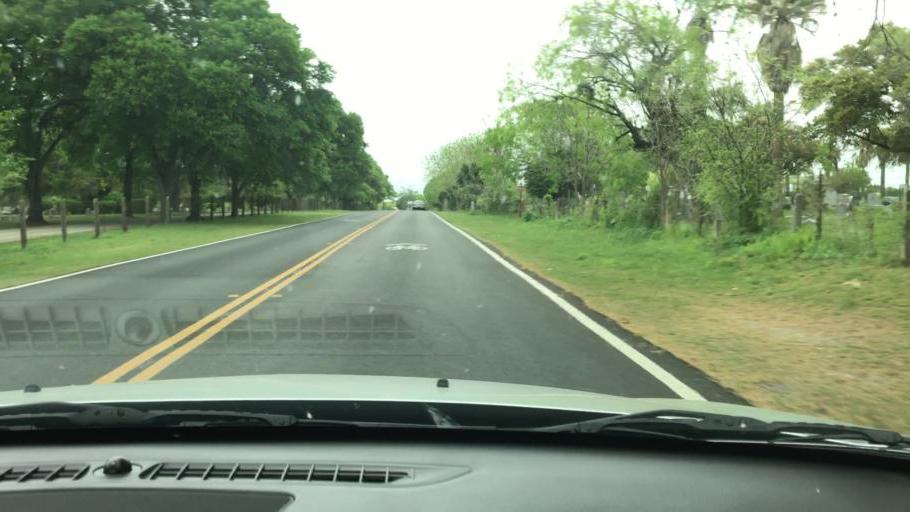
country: US
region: Texas
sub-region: Bexar County
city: San Antonio
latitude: 29.3454
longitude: -98.4717
